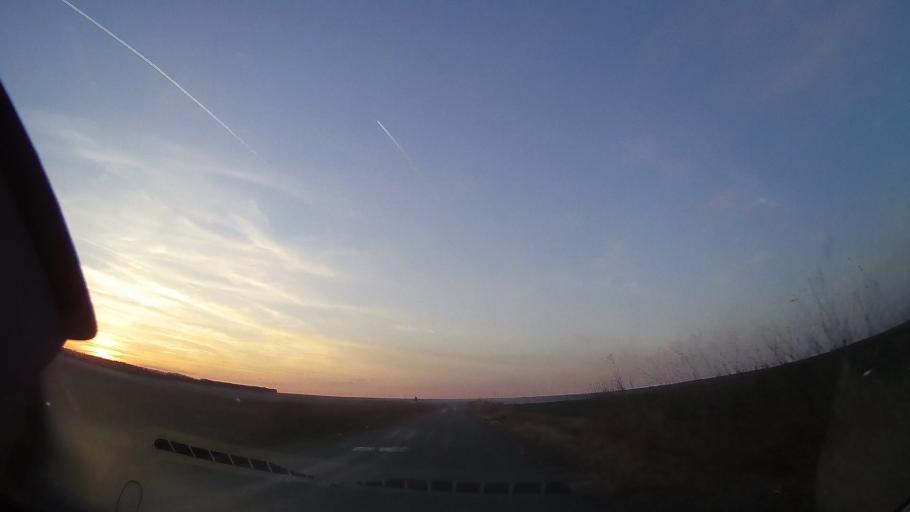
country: RO
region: Constanta
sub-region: Comuna Mereni
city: Mereni
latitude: 44.0160
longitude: 28.3091
